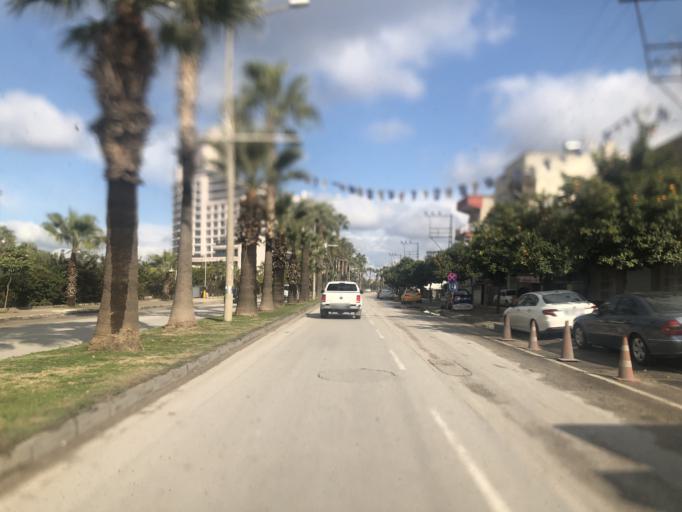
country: TR
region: Adana
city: Adana
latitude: 36.9925
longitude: 35.3395
